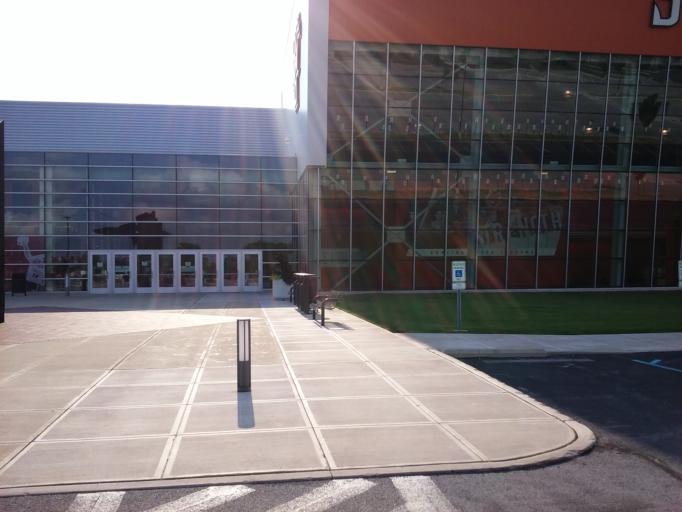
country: US
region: Ohio
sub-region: Wood County
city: Bowling Green
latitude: 41.3750
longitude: -83.6254
